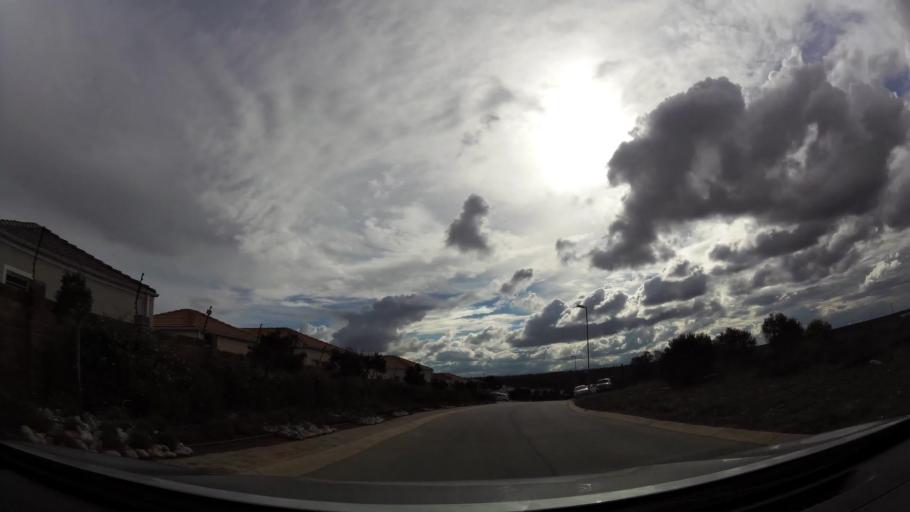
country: ZA
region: Eastern Cape
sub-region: Nelson Mandela Bay Metropolitan Municipality
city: Port Elizabeth
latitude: -33.9312
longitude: 25.5005
